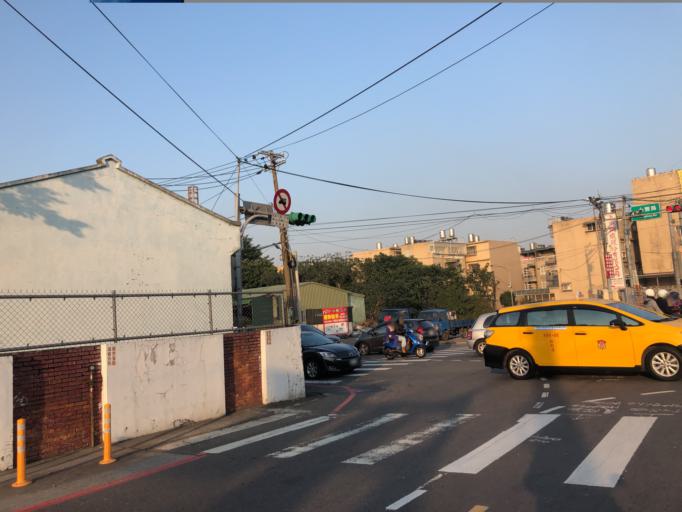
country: TW
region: Taiwan
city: Taoyuan City
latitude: 24.9606
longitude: 121.2790
